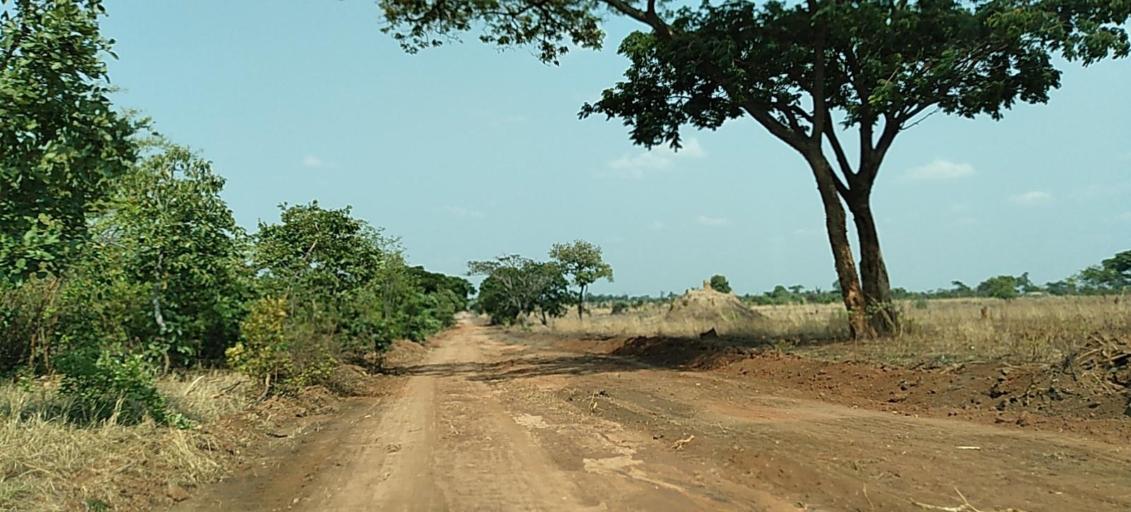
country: ZM
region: Copperbelt
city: Luanshya
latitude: -13.0901
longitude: 28.2738
